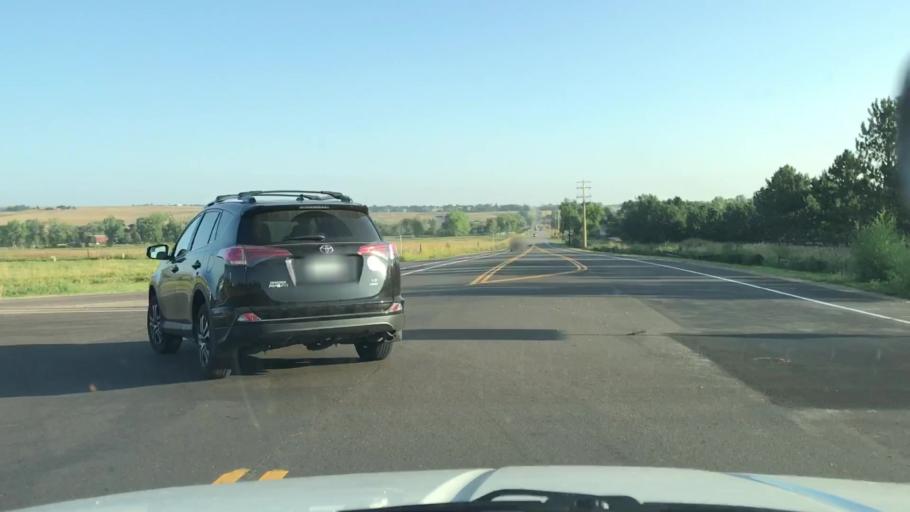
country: US
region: Colorado
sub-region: Boulder County
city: Gunbarrel
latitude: 40.0400
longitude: -105.1312
